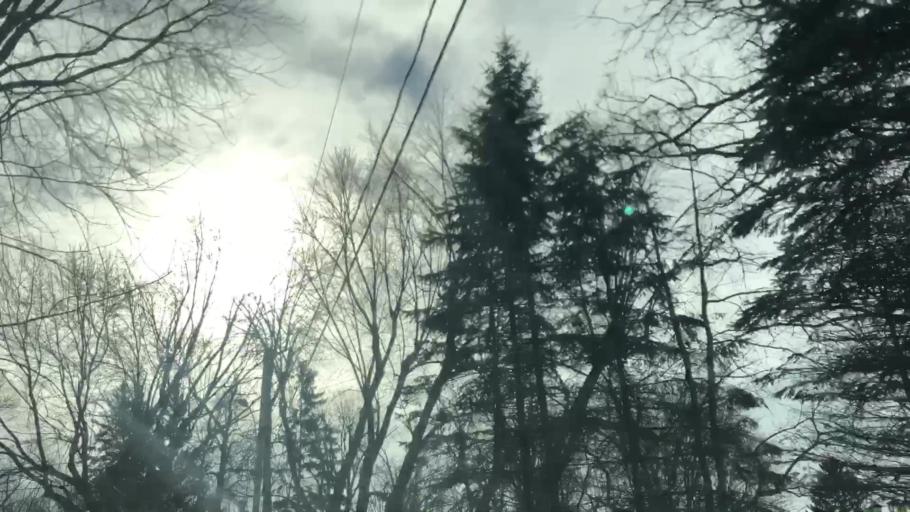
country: CA
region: Quebec
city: Sainte-Anne-de-Bellevue
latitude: 45.4154
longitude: -73.9636
